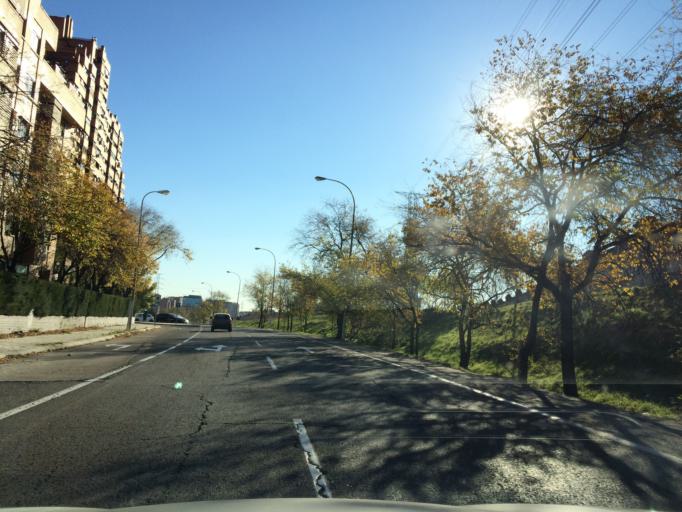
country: ES
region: Madrid
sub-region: Provincia de Madrid
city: Pinar de Chamartin
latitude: 40.4837
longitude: -3.6756
